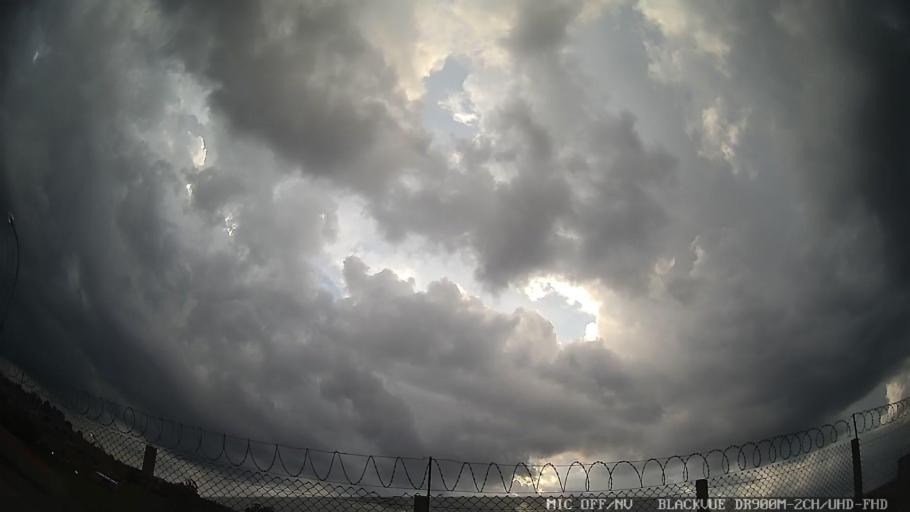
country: BR
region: Sao Paulo
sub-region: Braganca Paulista
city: Braganca Paulista
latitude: -22.9188
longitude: -46.5317
